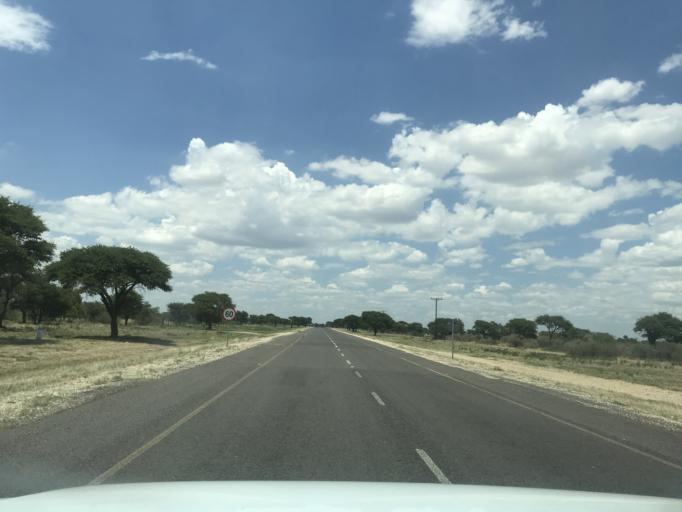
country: BW
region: South East
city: Janeng
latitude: -25.6371
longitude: 25.1524
